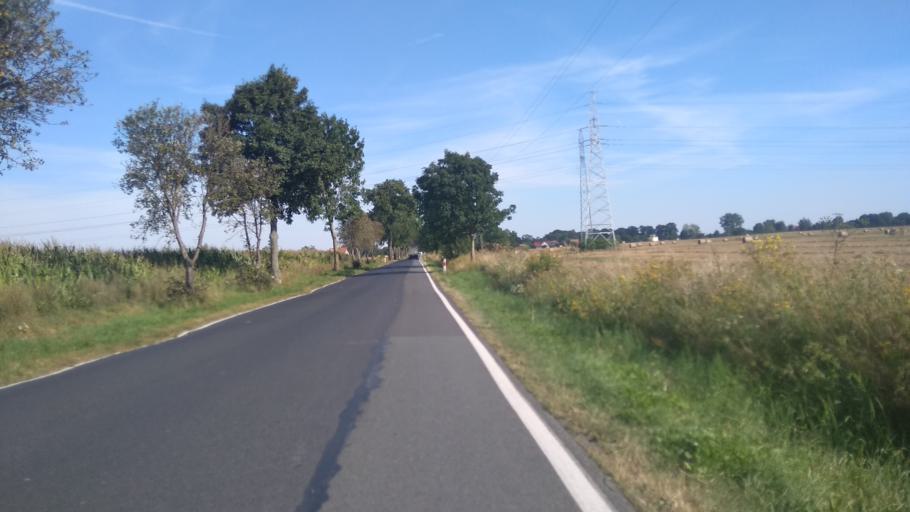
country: PL
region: Kujawsko-Pomorskie
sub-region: Powiat bydgoski
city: Osielsko
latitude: 53.2154
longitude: 18.1459
